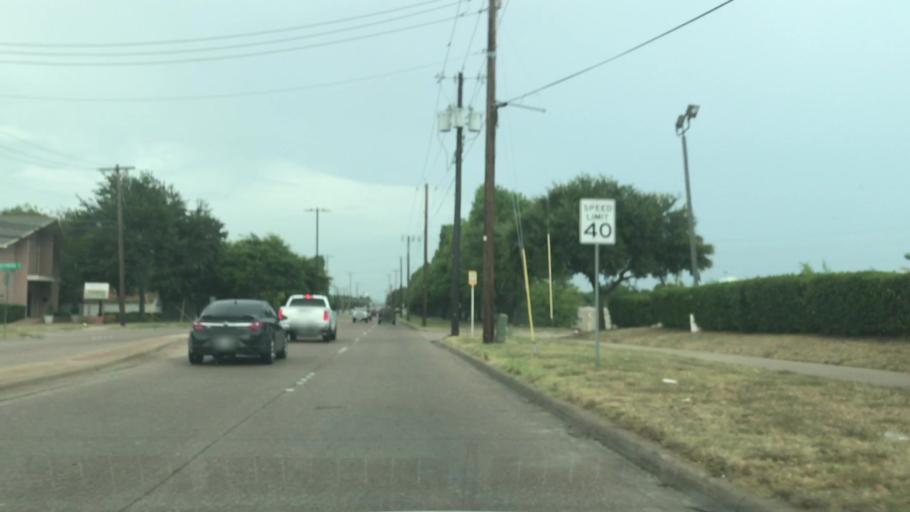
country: US
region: Texas
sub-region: Dallas County
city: Garland
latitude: 32.8788
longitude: -96.6652
